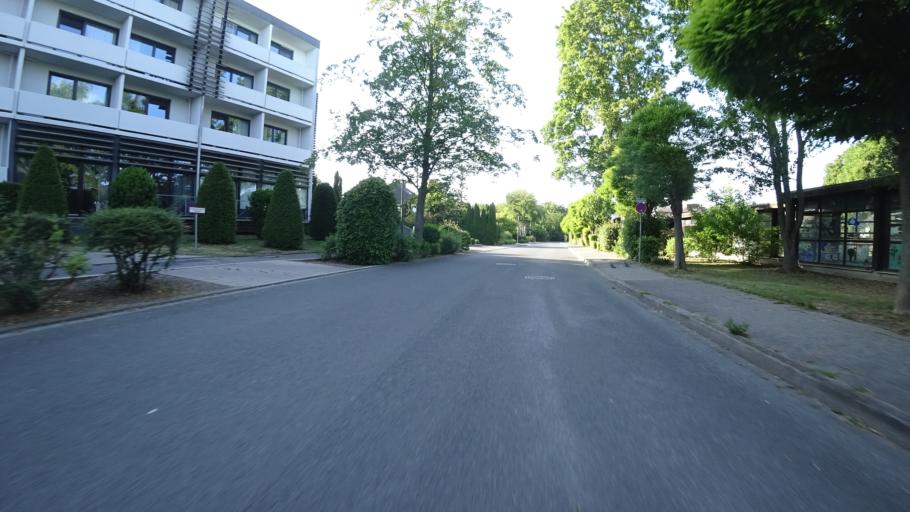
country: DE
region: North Rhine-Westphalia
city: Erwitte
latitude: 51.6304
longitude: 8.3540
